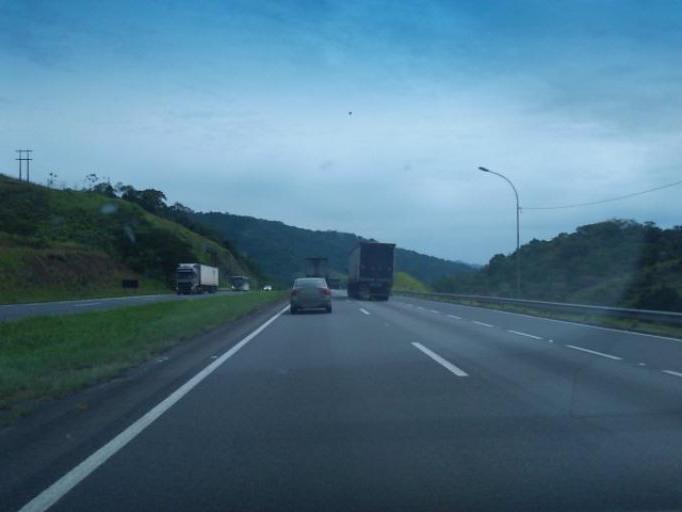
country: BR
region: Sao Paulo
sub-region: Miracatu
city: Miracatu
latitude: -24.2964
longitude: -47.4812
